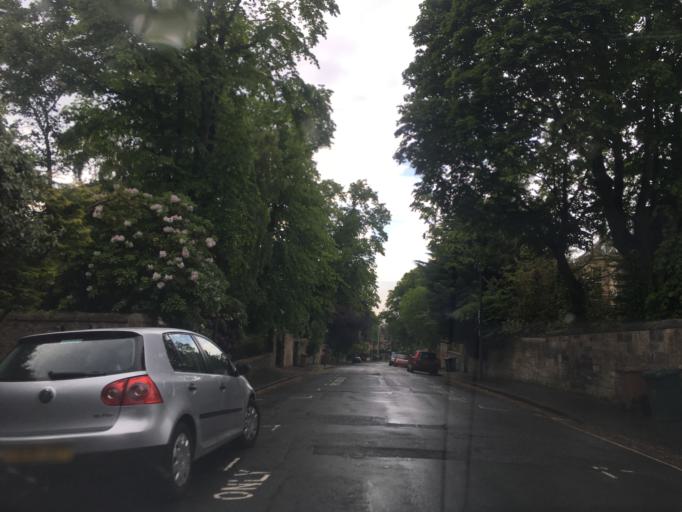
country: GB
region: Scotland
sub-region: Edinburgh
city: Edinburgh
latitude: 55.9336
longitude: -3.2203
